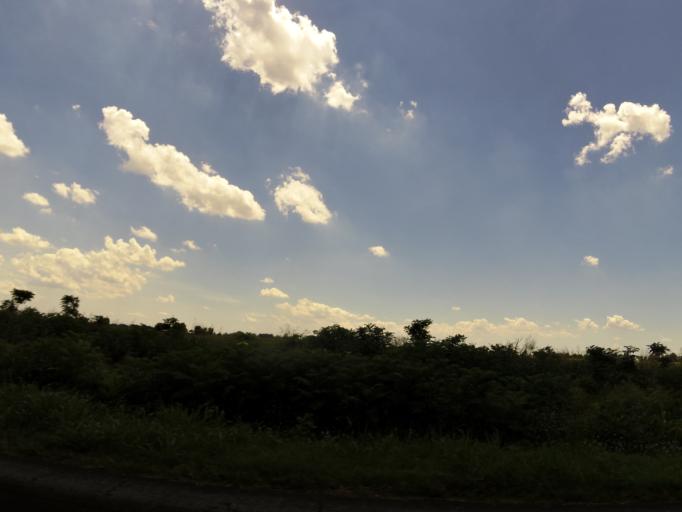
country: US
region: Missouri
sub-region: Pemiscot County
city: Caruthersville
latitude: 36.1680
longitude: -89.6854
